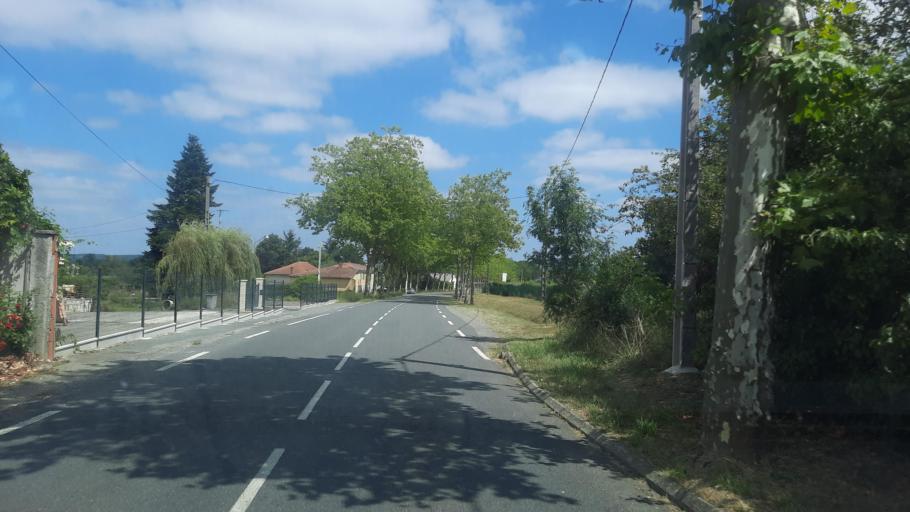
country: FR
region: Midi-Pyrenees
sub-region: Departement de la Haute-Garonne
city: Boulogne-sur-Gesse
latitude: 43.2924
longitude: 0.6510
